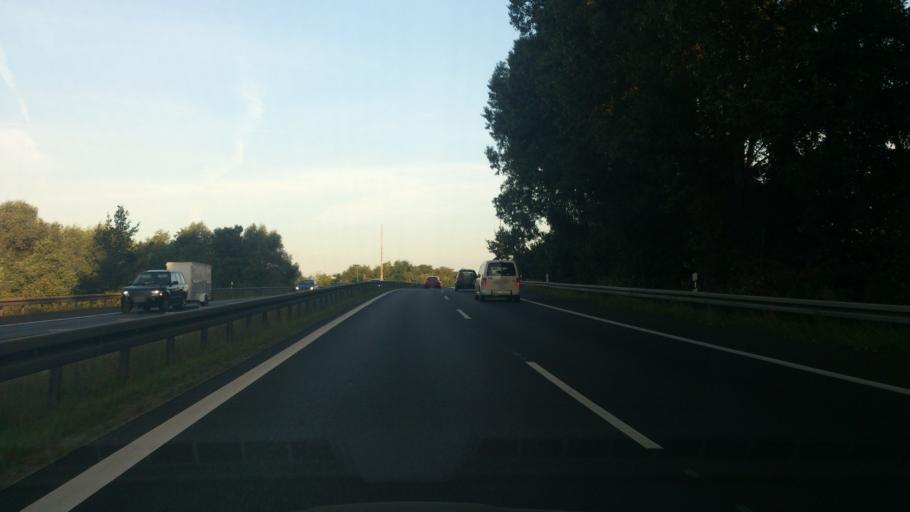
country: DE
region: Brandenburg
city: Potsdam
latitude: 52.3736
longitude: 13.1161
